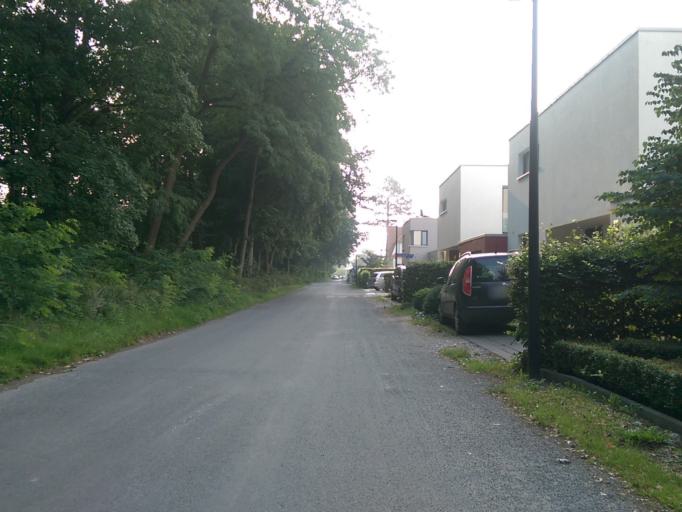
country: DE
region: North Rhine-Westphalia
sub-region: Regierungsbezirk Detmold
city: Guetersloh
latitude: 51.9004
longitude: 8.3505
